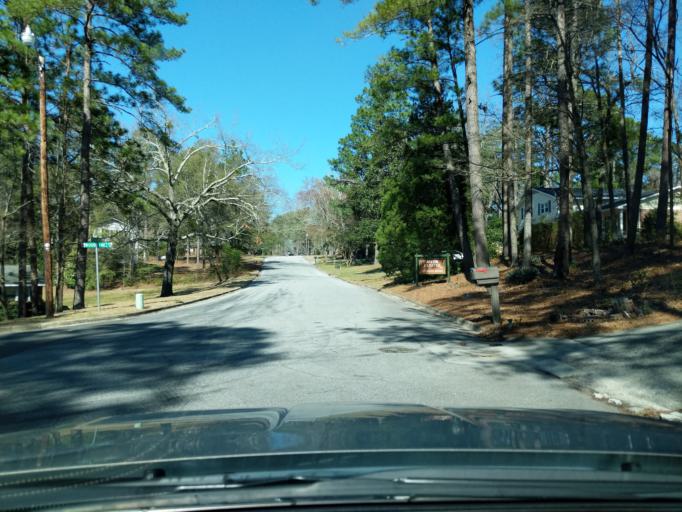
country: US
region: South Carolina
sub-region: Aiken County
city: Aiken
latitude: 33.5341
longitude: -81.7398
